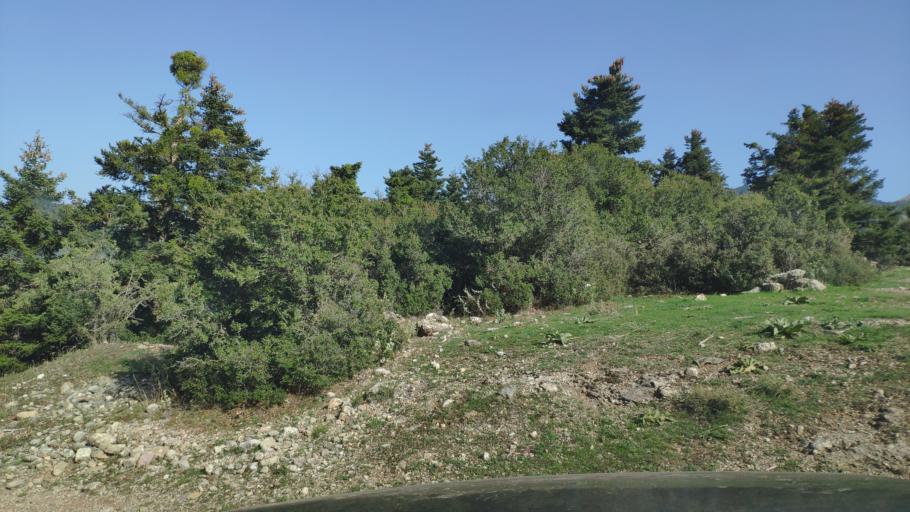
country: GR
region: West Greece
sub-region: Nomos Achaias
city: Aiyira
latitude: 37.9804
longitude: 22.3449
